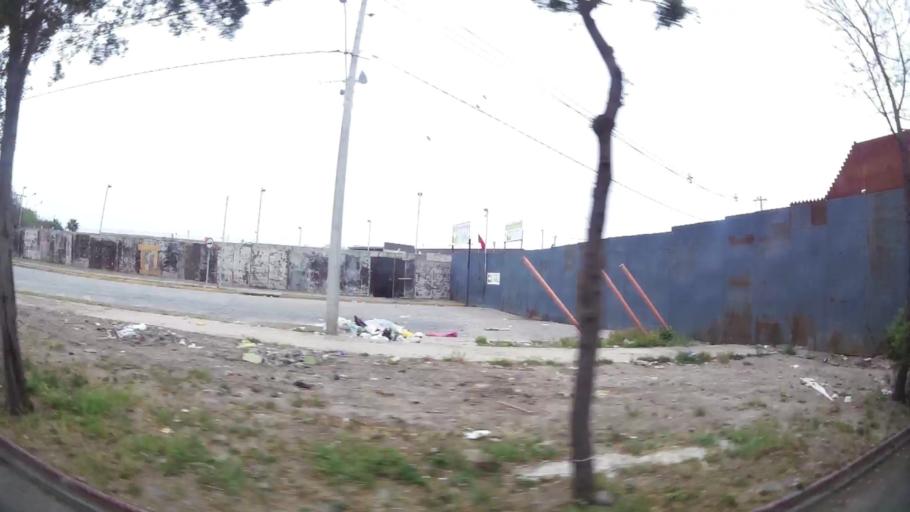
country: CL
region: Santiago Metropolitan
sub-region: Provincia de Santiago
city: Santiago
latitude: -33.4860
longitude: -70.6352
